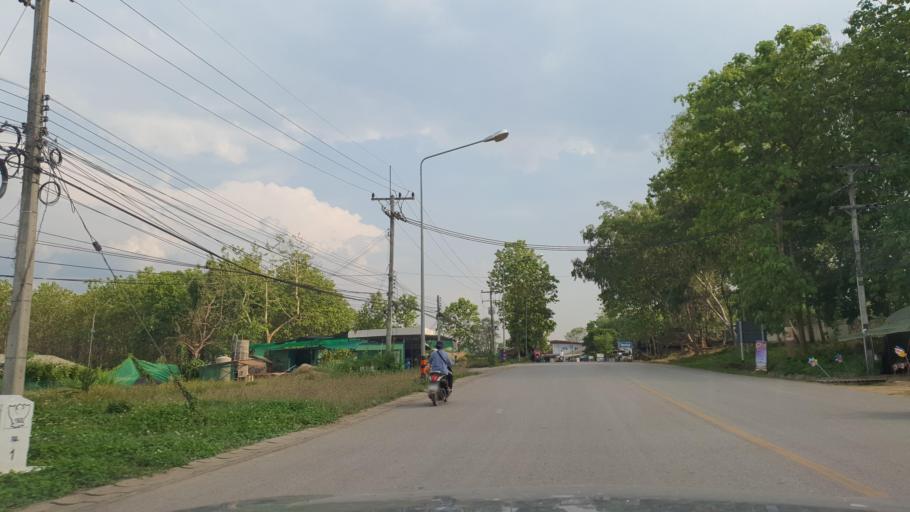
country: TH
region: Chiang Mai
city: Pai
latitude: 19.3545
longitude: 98.4350
